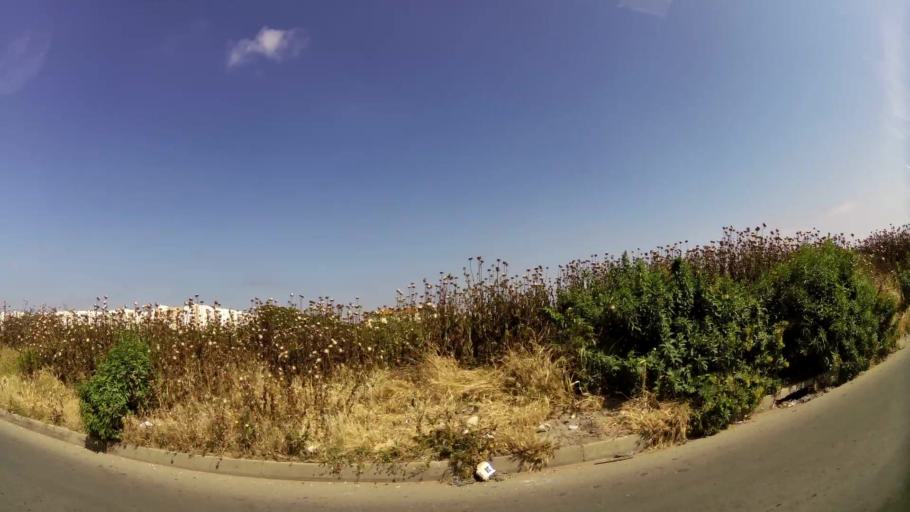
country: MA
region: Rabat-Sale-Zemmour-Zaer
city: Sale
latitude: 34.0802
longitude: -6.7571
